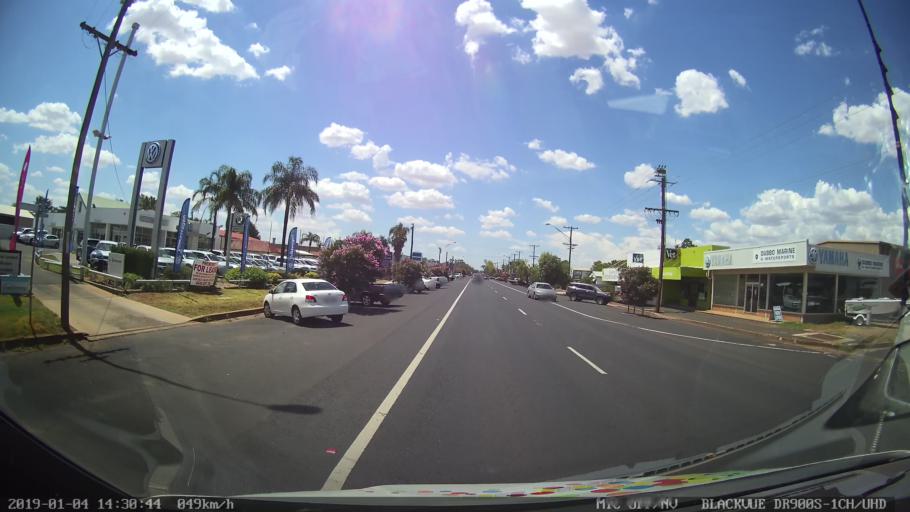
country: AU
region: New South Wales
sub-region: Dubbo Municipality
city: Dubbo
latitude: -32.2370
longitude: 148.6107
